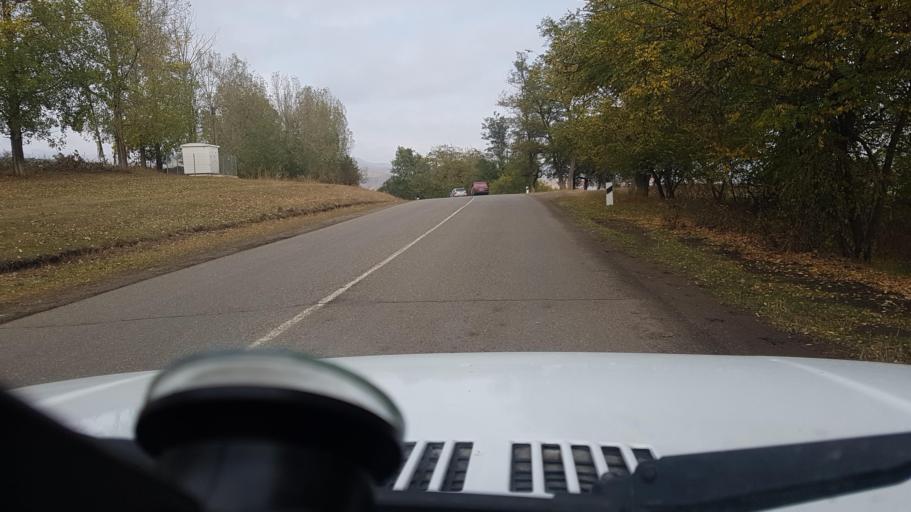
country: AZ
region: Gadabay Rayon
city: Ariqdam
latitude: 40.6448
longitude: 45.8128
